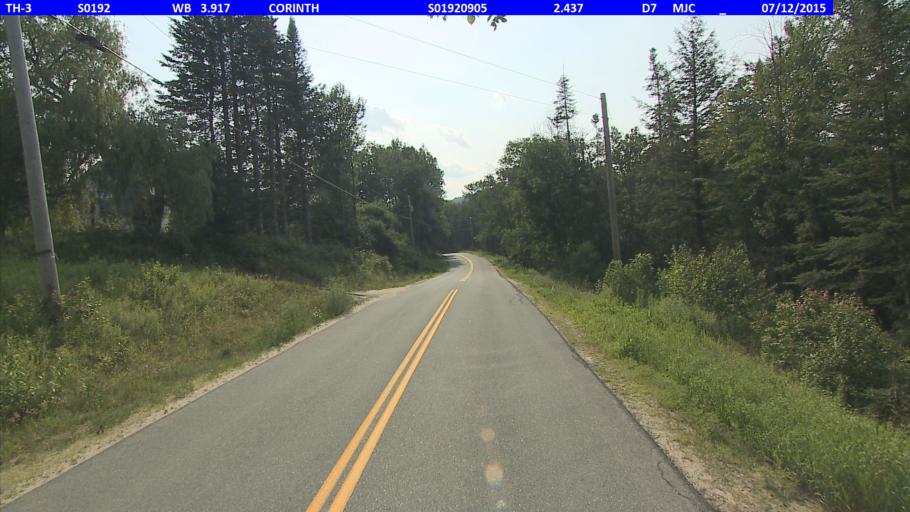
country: US
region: Vermont
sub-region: Orange County
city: Chelsea
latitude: 44.0019
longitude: -72.3116
